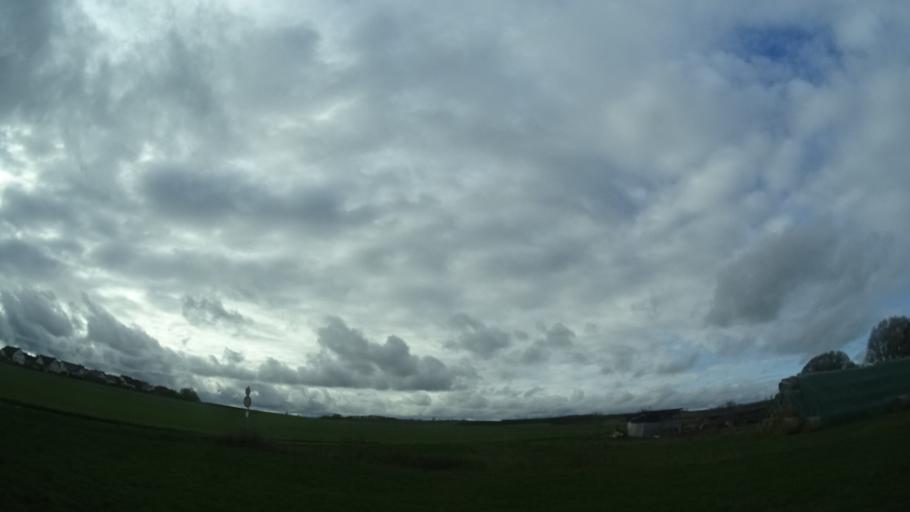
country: DE
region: Bavaria
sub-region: Regierungsbezirk Unterfranken
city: Hochheim
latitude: 50.3690
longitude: 10.4697
